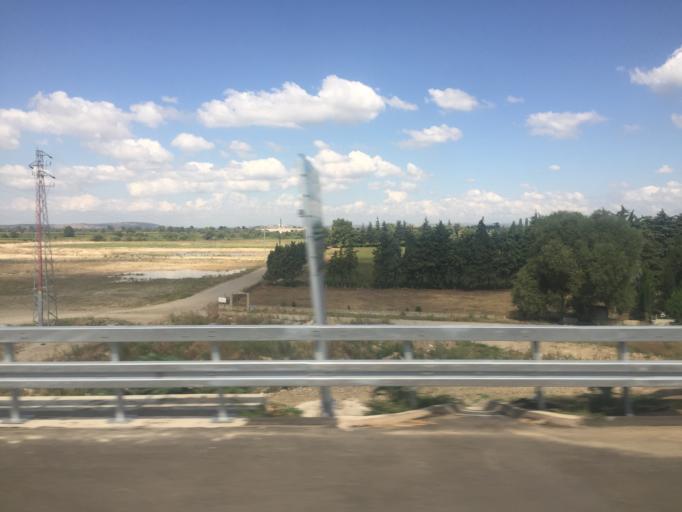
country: TR
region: Balikesir
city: Gobel
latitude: 40.0696
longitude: 28.2498
